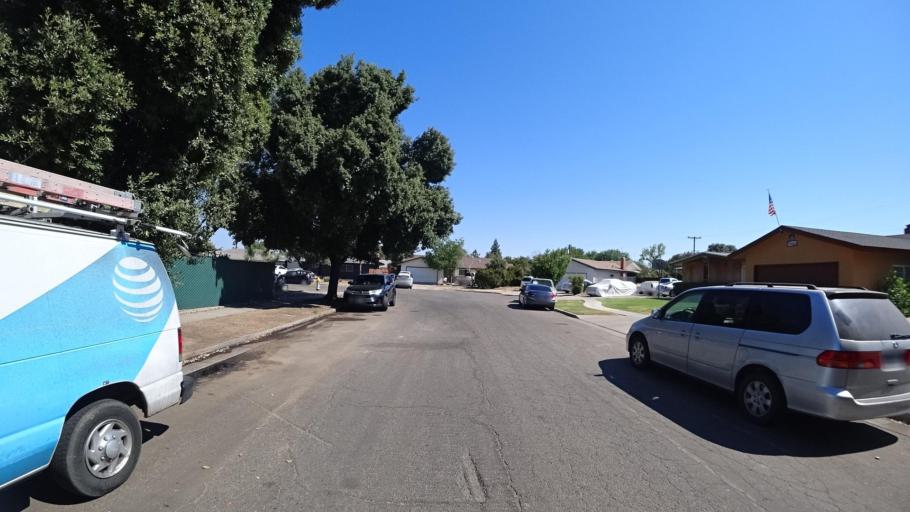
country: US
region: California
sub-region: Fresno County
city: Fresno
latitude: 36.7677
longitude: -119.7383
